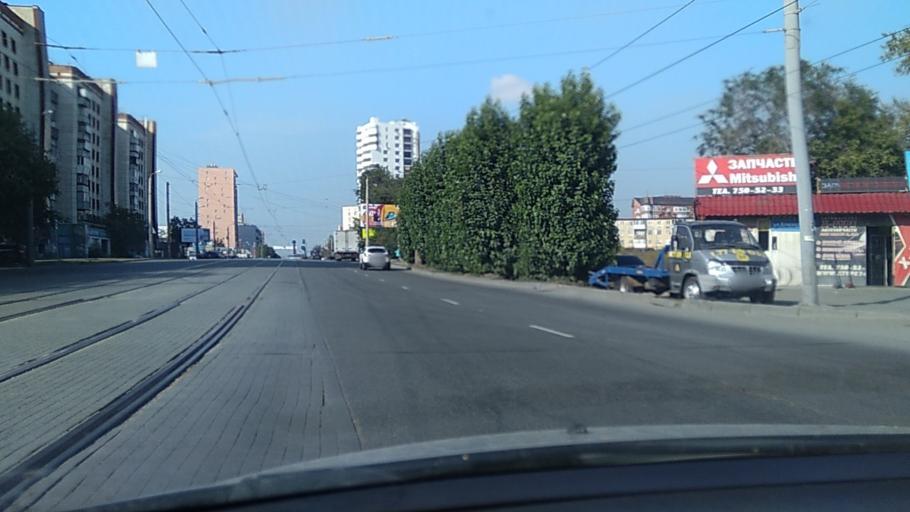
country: RU
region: Chelyabinsk
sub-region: Gorod Chelyabinsk
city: Chelyabinsk
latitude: 55.1472
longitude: 61.3899
